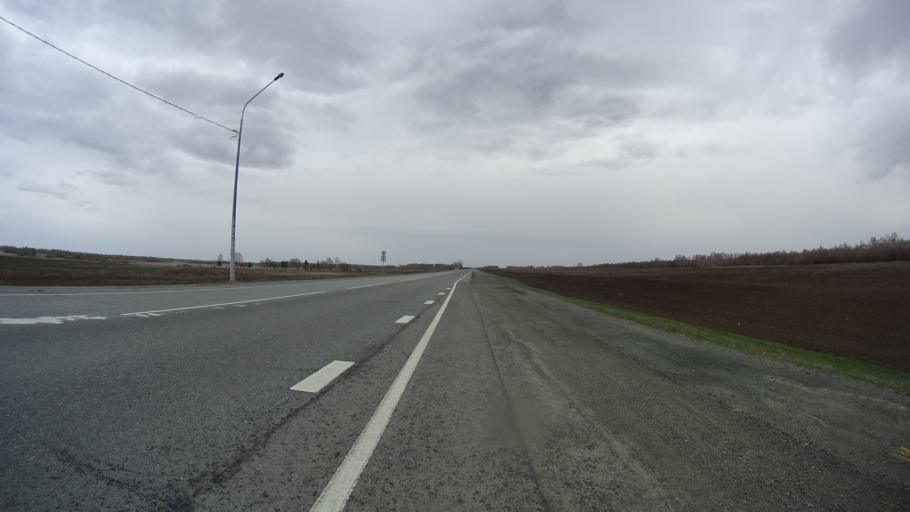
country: RU
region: Chelyabinsk
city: Krasnogorskiy
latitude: 54.6708
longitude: 61.2506
